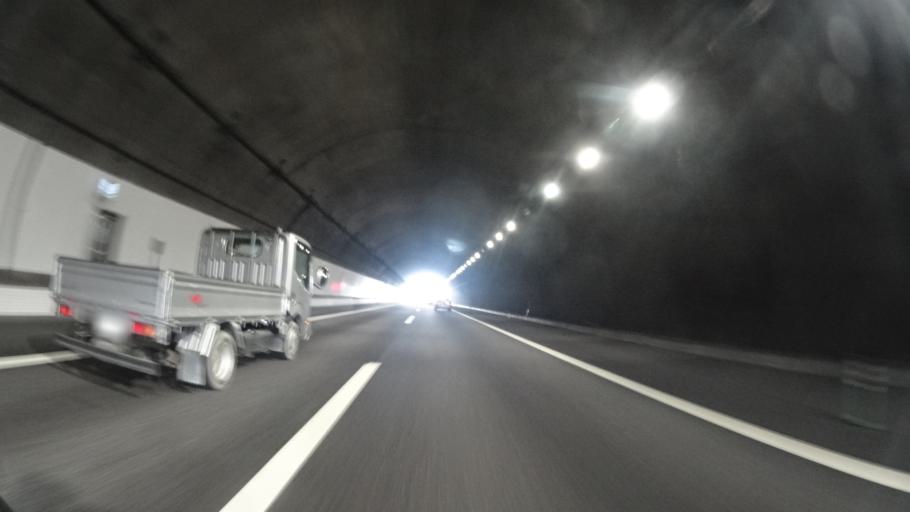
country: JP
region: Shiga Prefecture
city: Minakuchicho-matoba
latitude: 34.9226
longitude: 136.1106
